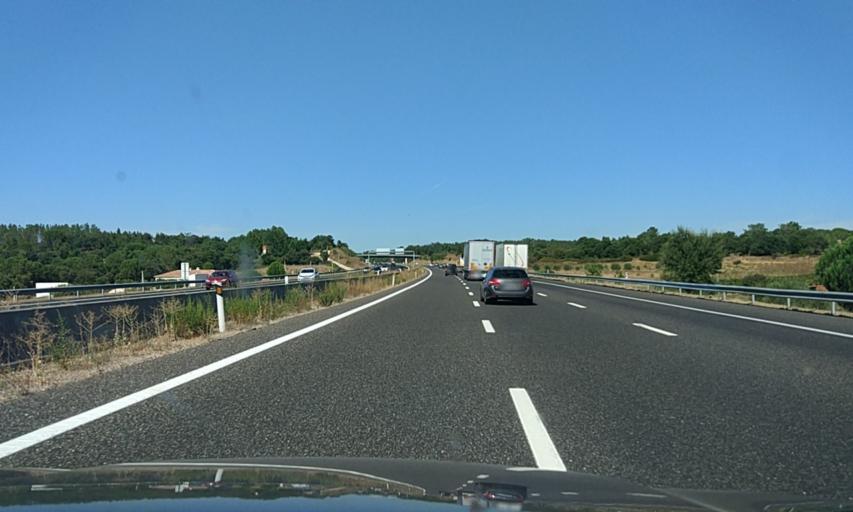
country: PT
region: Santarem
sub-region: Cartaxo
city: Cartaxo
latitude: 39.2130
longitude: -8.7804
